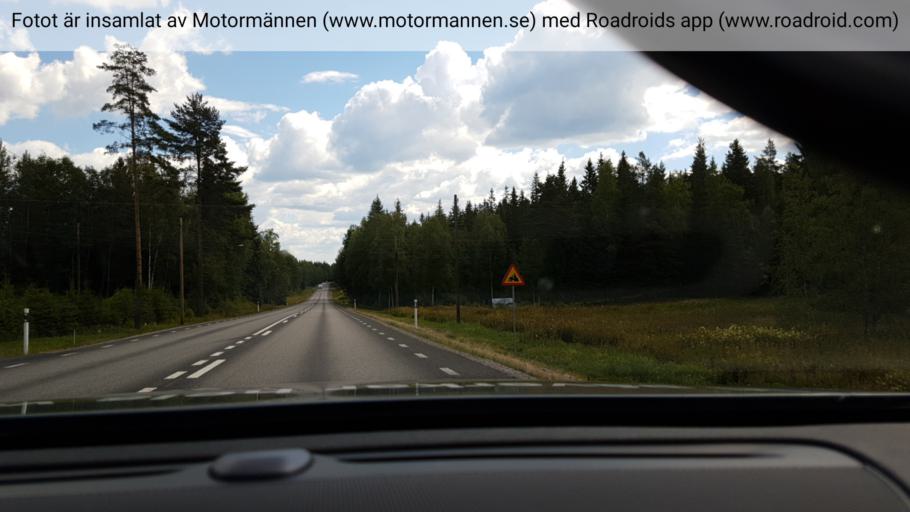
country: SE
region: Dalarna
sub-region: Faluns Kommun
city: Bjursas
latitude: 60.7410
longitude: 15.4108
